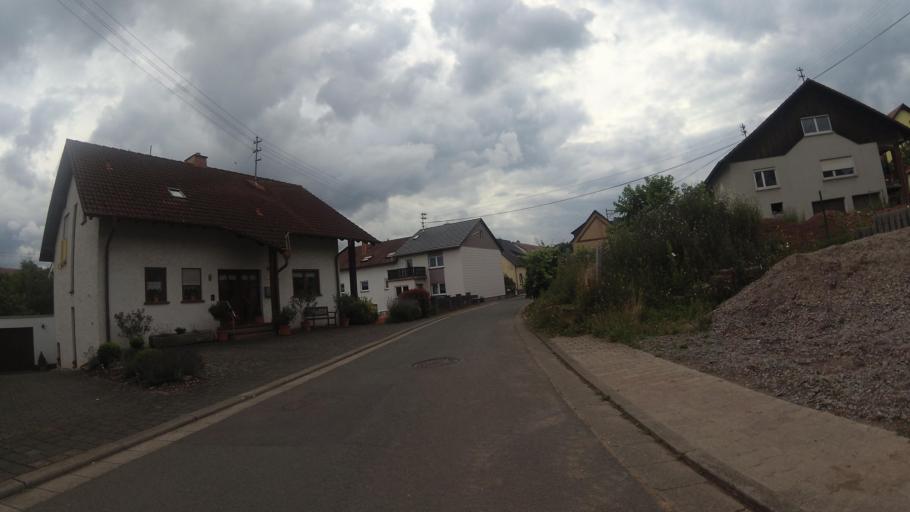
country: DE
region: Rheinland-Pfalz
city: Krottelbach
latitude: 49.4672
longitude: 7.3276
